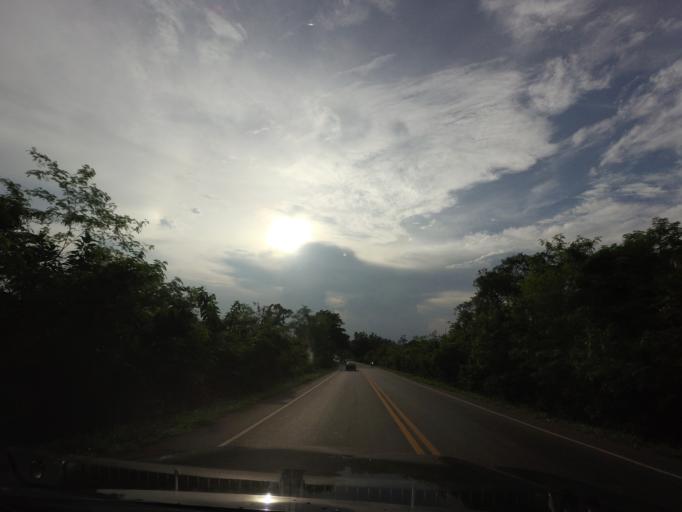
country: TH
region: Nong Khai
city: Pho Tak
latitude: 17.8037
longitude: 102.3173
